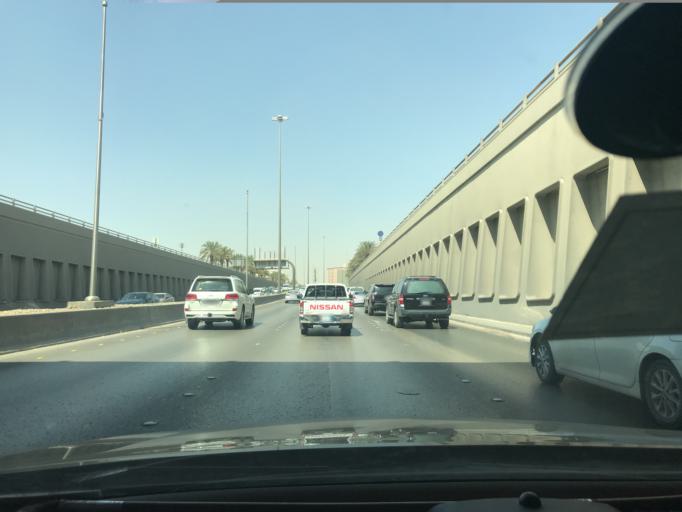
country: SA
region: Ar Riyad
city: Riyadh
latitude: 24.6686
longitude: 46.6955
